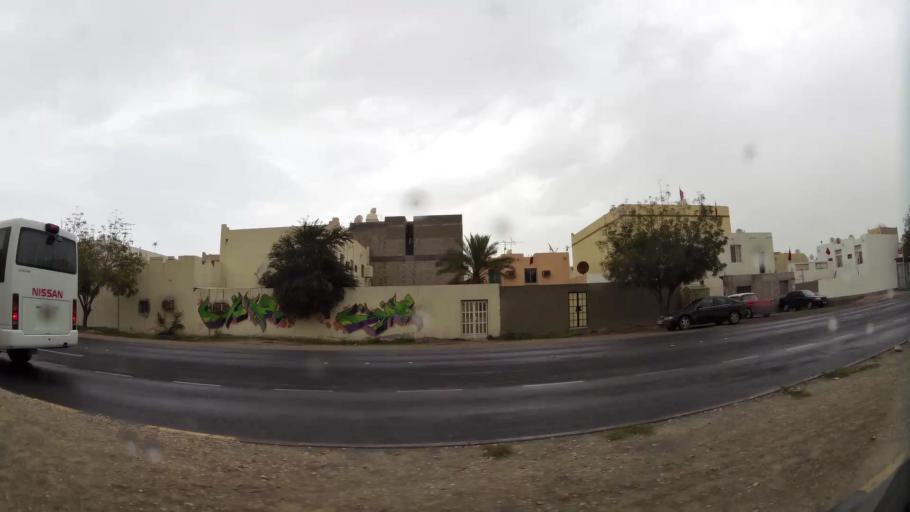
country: BH
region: Northern
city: Ar Rifa'
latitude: 26.1378
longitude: 50.5673
